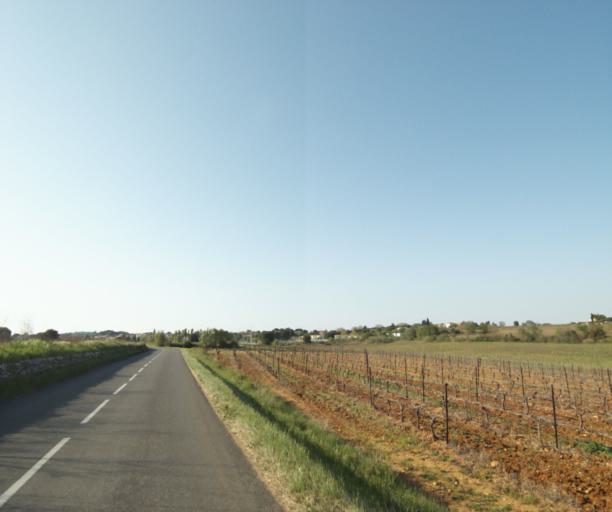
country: FR
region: Languedoc-Roussillon
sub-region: Departement de l'Herault
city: Laverune
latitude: 43.6026
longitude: 3.7883
